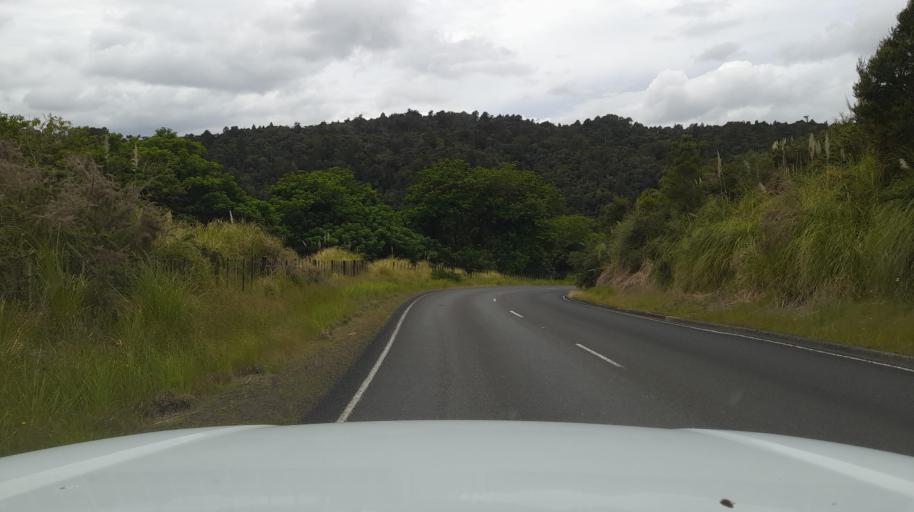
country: NZ
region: Northland
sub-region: Far North District
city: Kaitaia
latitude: -35.3574
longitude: 173.4634
